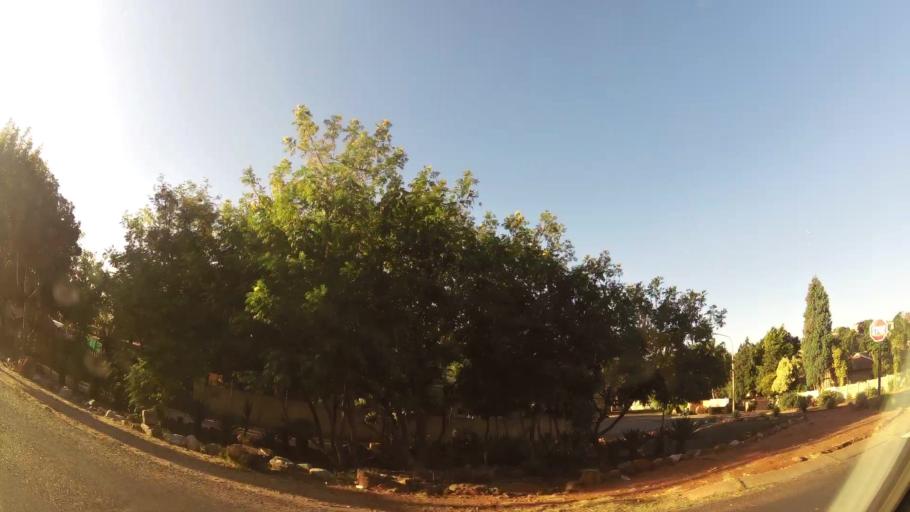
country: ZA
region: North-West
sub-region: Bojanala Platinum District Municipality
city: Rustenburg
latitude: -25.7050
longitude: 27.2379
